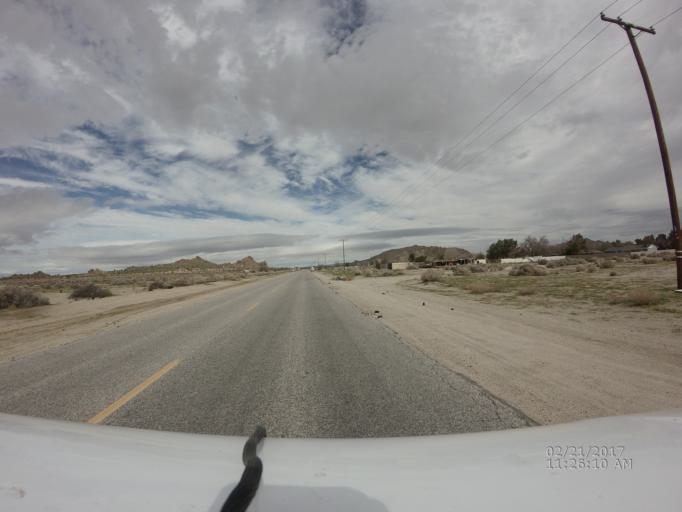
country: US
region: California
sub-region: Los Angeles County
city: Lake Los Angeles
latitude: 34.6320
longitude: -117.8628
